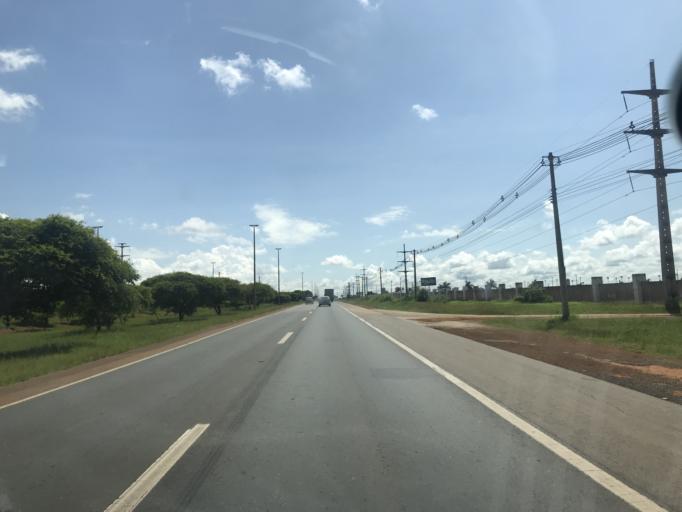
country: BR
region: Federal District
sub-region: Brasilia
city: Brasilia
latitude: -15.8859
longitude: -48.0711
